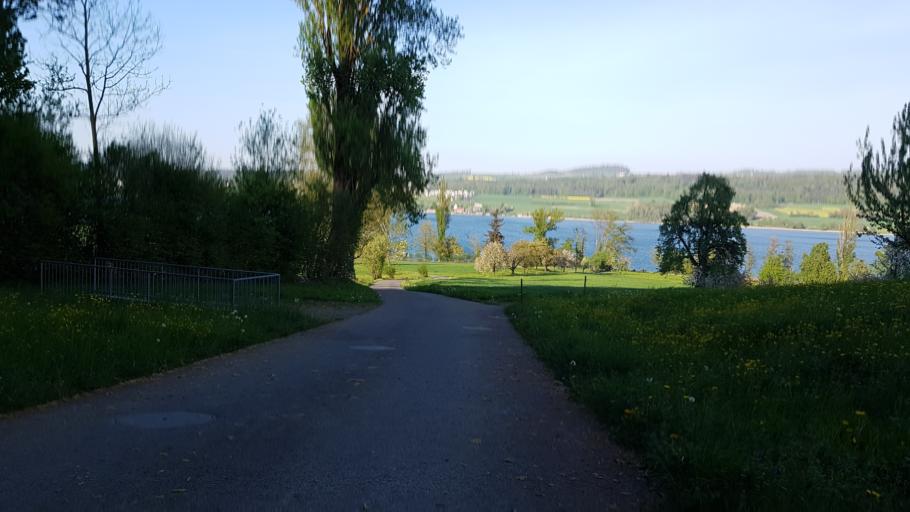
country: CH
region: Aargau
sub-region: Bezirk Kulm
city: Reinach
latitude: 47.2733
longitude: 8.2050
